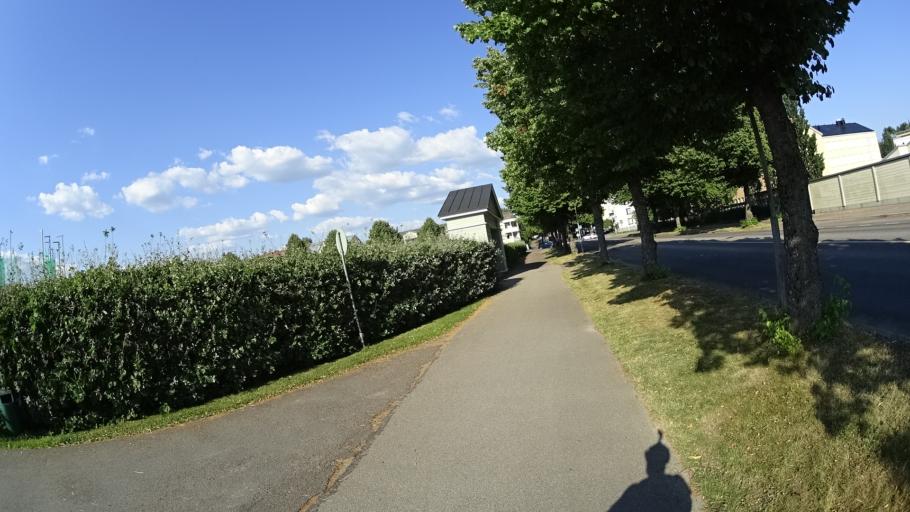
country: FI
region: Uusimaa
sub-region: Porvoo
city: Porvoo
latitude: 60.3929
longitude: 25.6731
